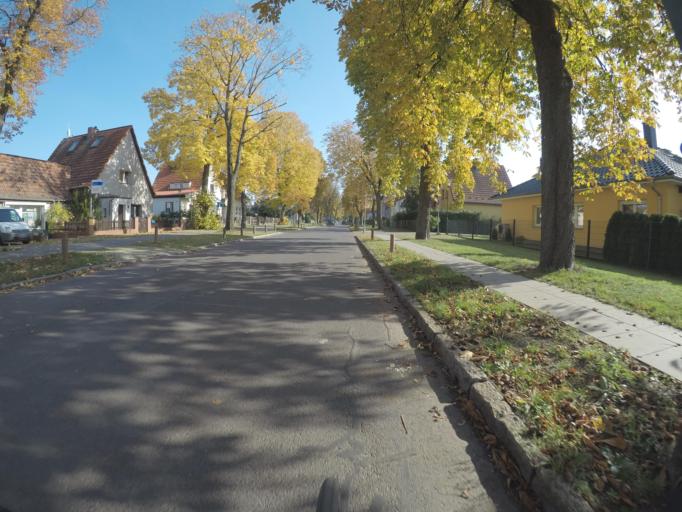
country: DE
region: Brandenburg
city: Hohen Neuendorf
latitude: 52.6802
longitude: 13.2492
